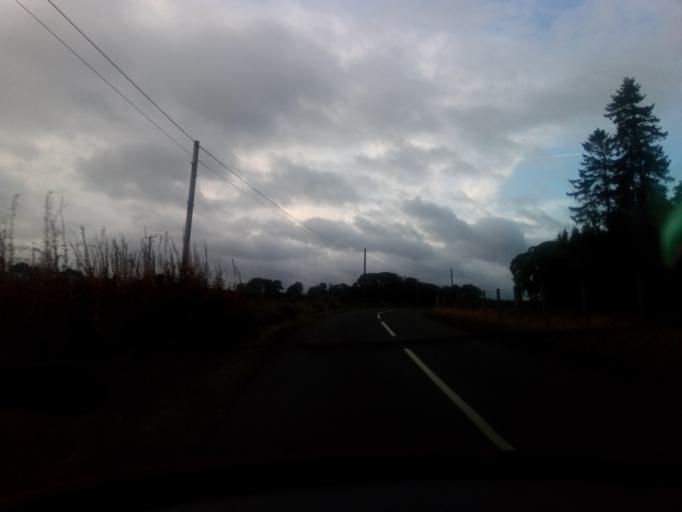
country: GB
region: Scotland
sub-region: The Scottish Borders
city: Jedburgh
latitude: 55.4186
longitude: -2.6315
